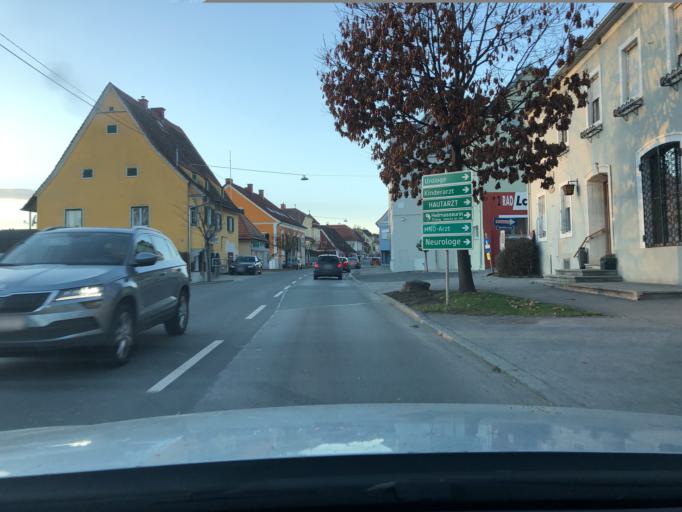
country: AT
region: Styria
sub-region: Politischer Bezirk Weiz
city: Gleisdorf
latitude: 47.1023
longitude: 15.7136
